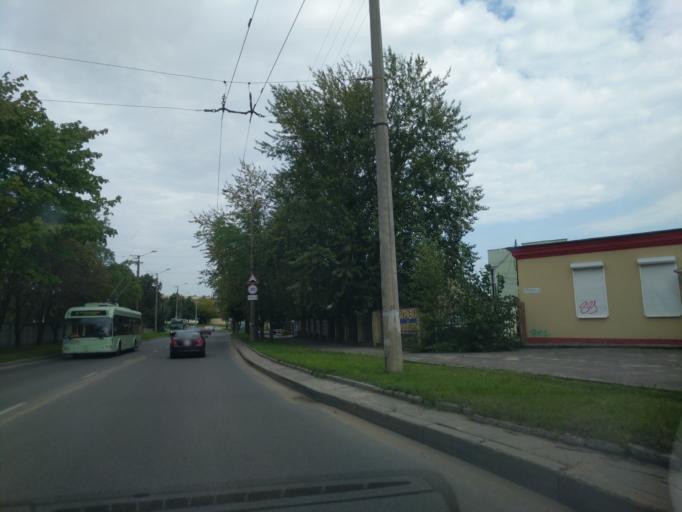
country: BY
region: Minsk
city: Novoye Medvezhino
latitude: 53.8901
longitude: 27.4815
